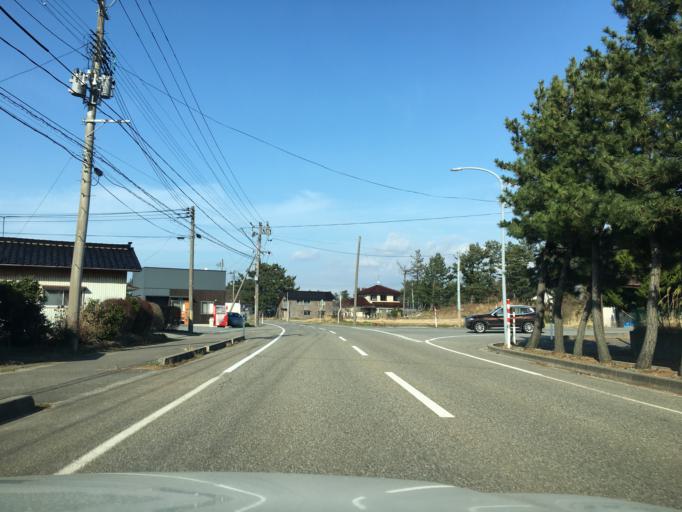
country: JP
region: Yamagata
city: Tsuruoka
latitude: 38.7910
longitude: 139.7679
